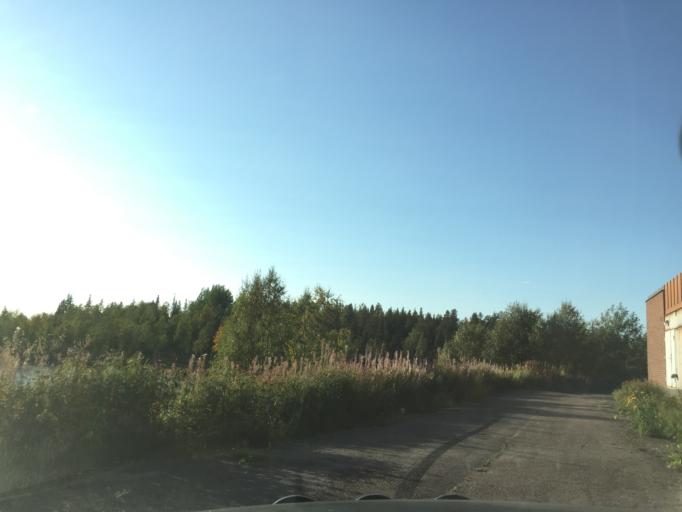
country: SE
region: Norrbotten
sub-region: Gallivare Kommun
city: Malmberget
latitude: 67.6536
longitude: 21.0371
